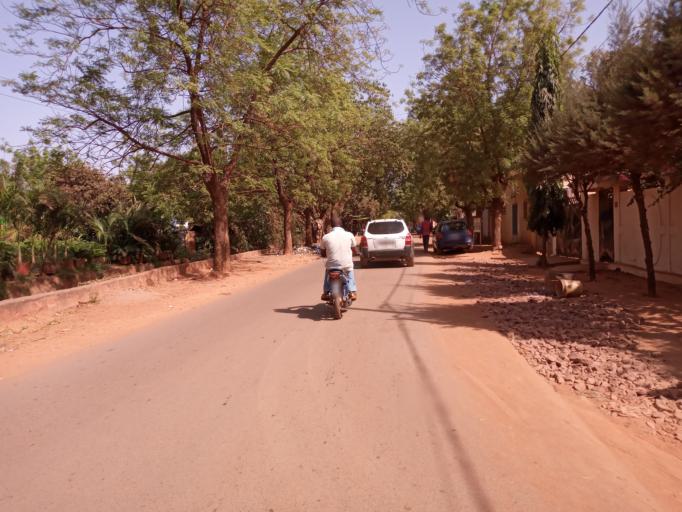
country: ML
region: Bamako
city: Bamako
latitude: 12.5910
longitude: -7.9523
